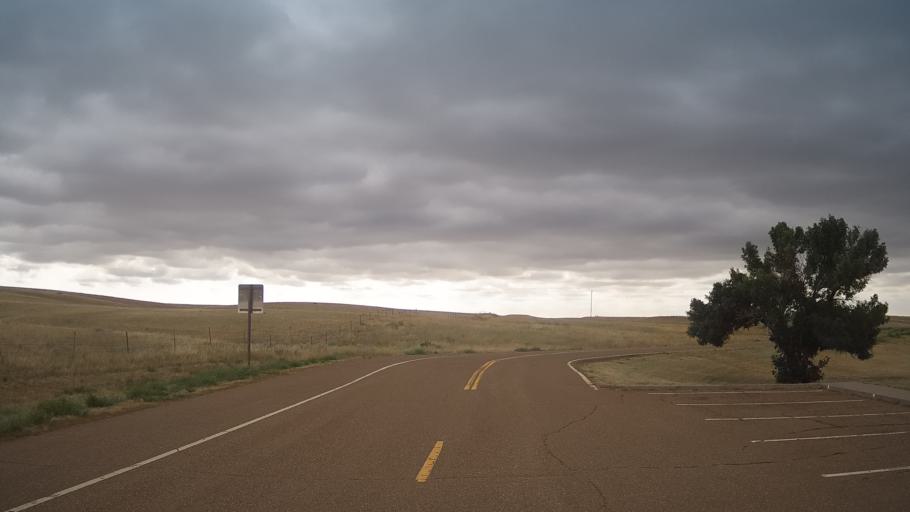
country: US
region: Montana
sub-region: Valley County
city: Glasgow
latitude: 48.3701
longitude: -106.7927
